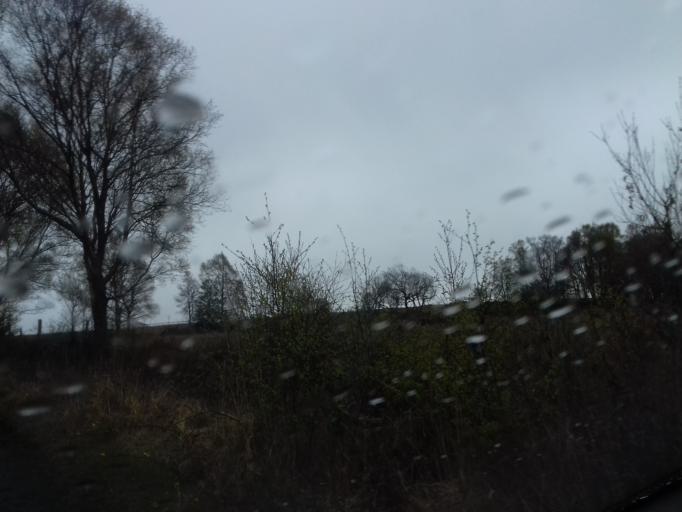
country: IE
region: Connaught
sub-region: County Leitrim
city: Manorhamilton
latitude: 54.2620
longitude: -7.9306
